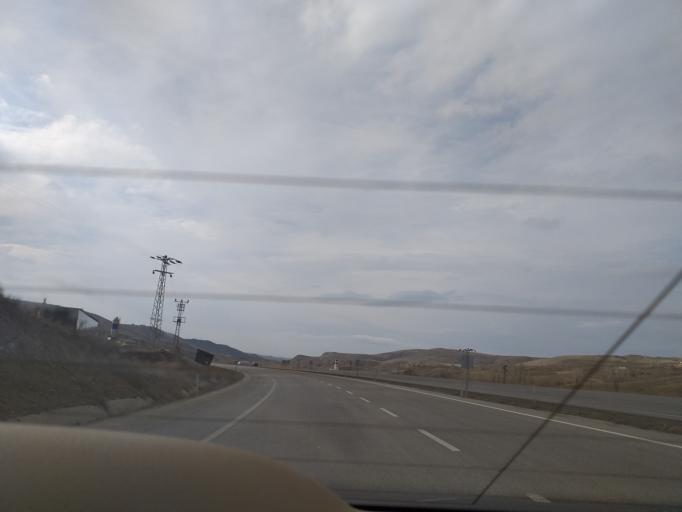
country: TR
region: Yozgat
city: Yozgat
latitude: 39.7942
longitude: 34.7594
